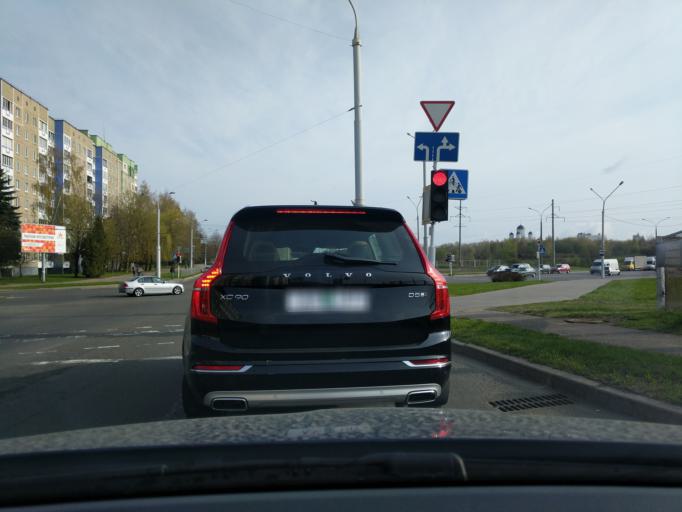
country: BY
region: Minsk
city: Novoye Medvezhino
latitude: 53.8990
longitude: 27.4633
